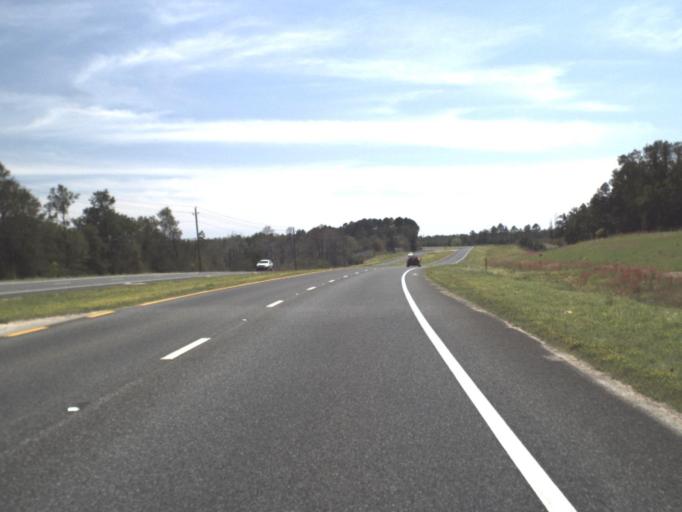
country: US
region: Florida
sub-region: Bay County
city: Lynn Haven
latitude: 30.4245
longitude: -85.6880
